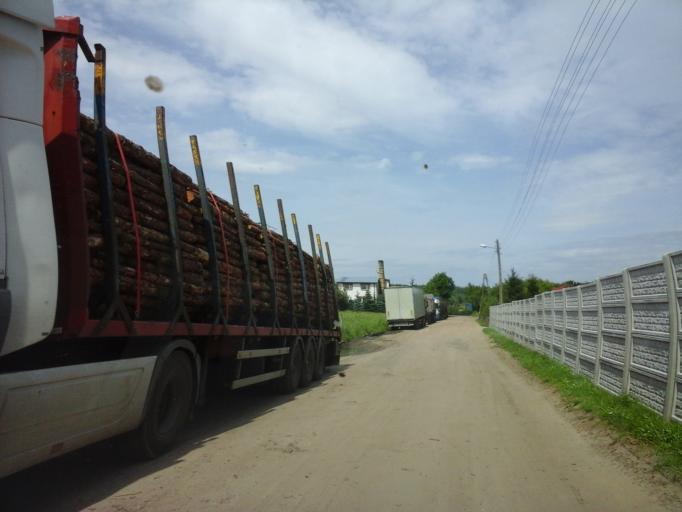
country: PL
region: Lubusz
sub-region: Powiat strzelecko-drezdenecki
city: Dobiegniew
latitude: 53.0530
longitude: 15.7473
